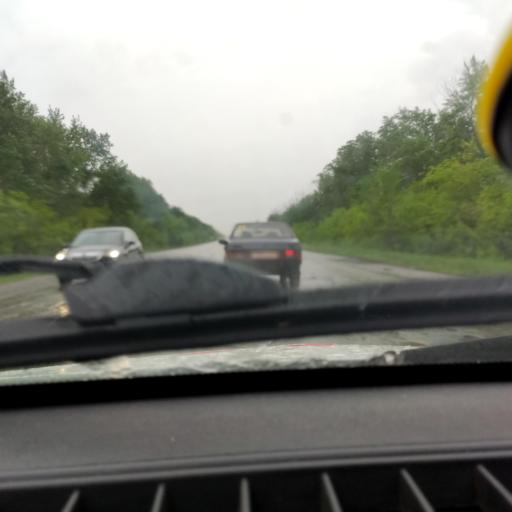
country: RU
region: Samara
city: Tol'yatti
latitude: 53.6149
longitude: 49.4129
